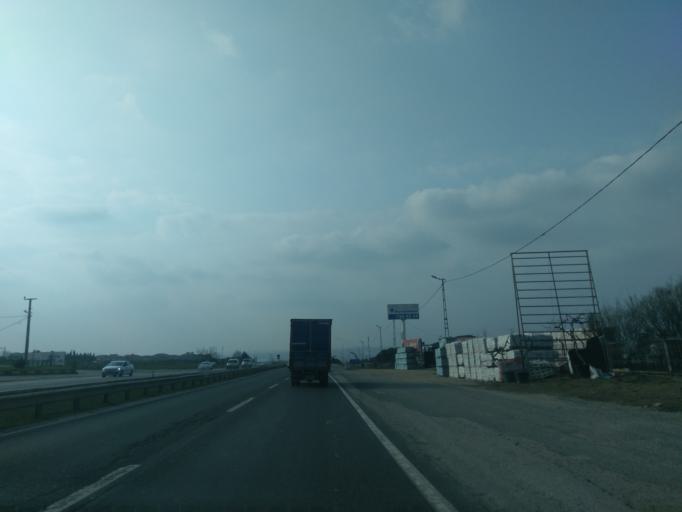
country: TR
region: Istanbul
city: Silivri
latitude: 41.0725
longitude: 28.2721
